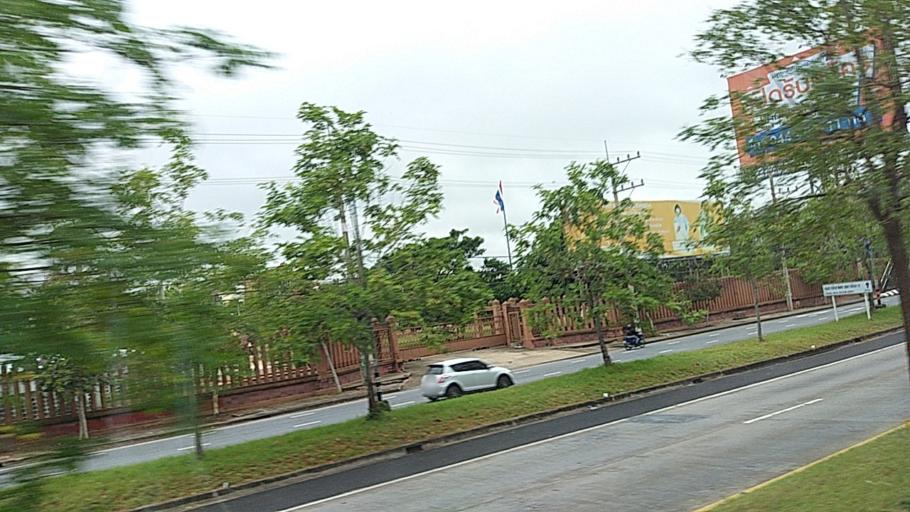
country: TH
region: Nakhon Ratchasima
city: Nakhon Ratchasima
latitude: 15.0004
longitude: 102.1182
